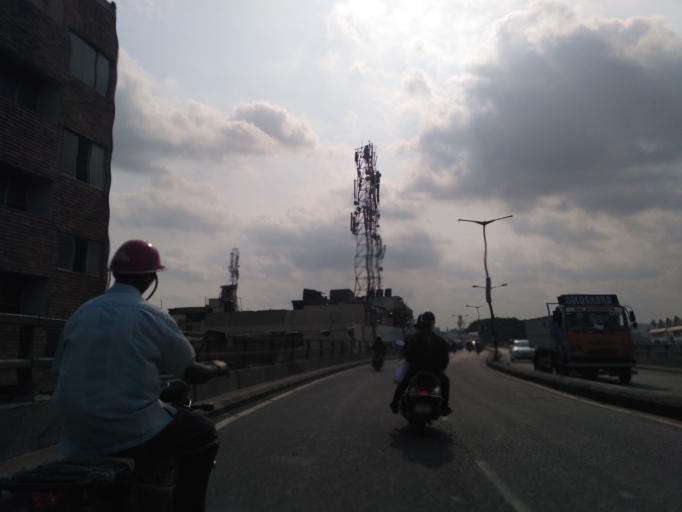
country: IN
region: Karnataka
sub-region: Bangalore Urban
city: Bangalore
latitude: 12.9636
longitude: 77.5785
